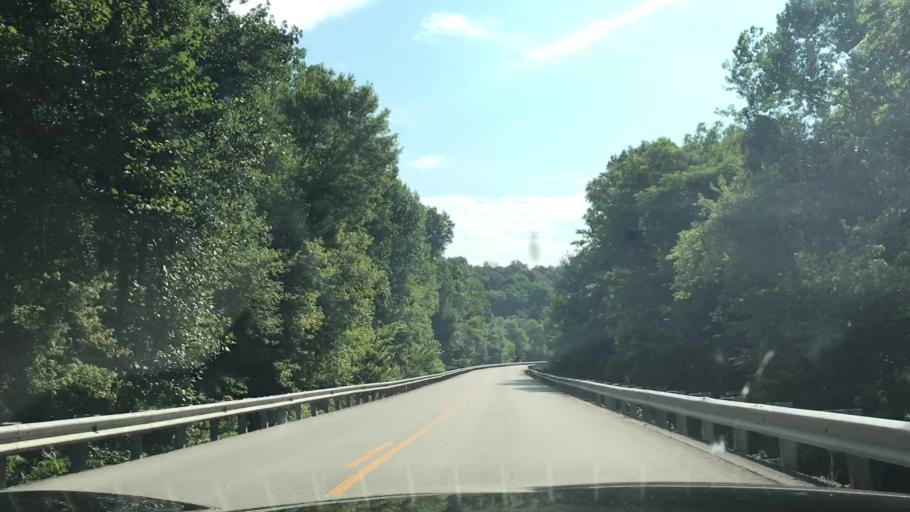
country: US
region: Kentucky
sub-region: Green County
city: Greensburg
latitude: 37.2267
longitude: -85.6761
